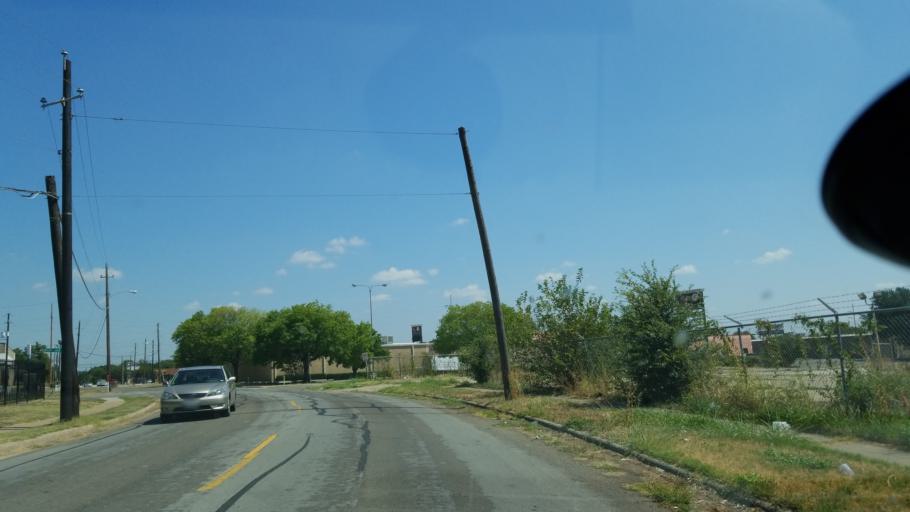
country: US
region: Texas
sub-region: Dallas County
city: Duncanville
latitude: 32.6601
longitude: -96.8842
